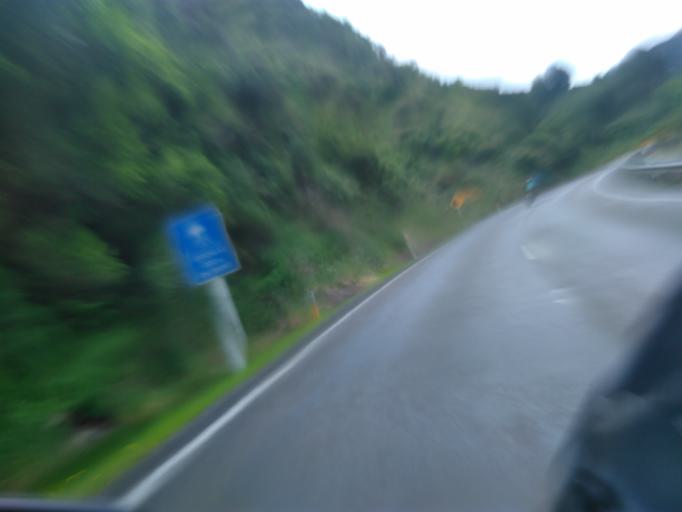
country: NZ
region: Bay of Plenty
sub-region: Opotiki District
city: Opotiki
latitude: -38.2538
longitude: 177.3002
